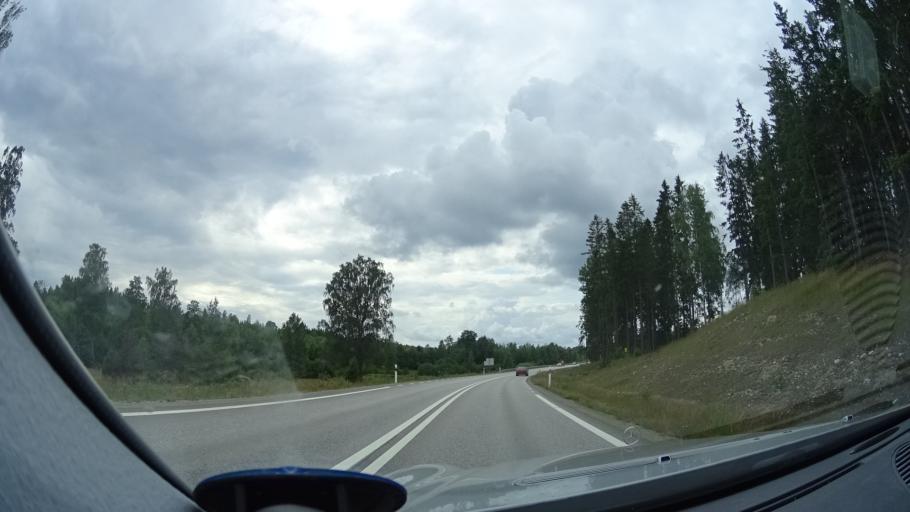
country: SE
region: Kronoberg
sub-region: Tingsryds Kommun
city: Tingsryd
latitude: 56.5019
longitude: 15.0411
